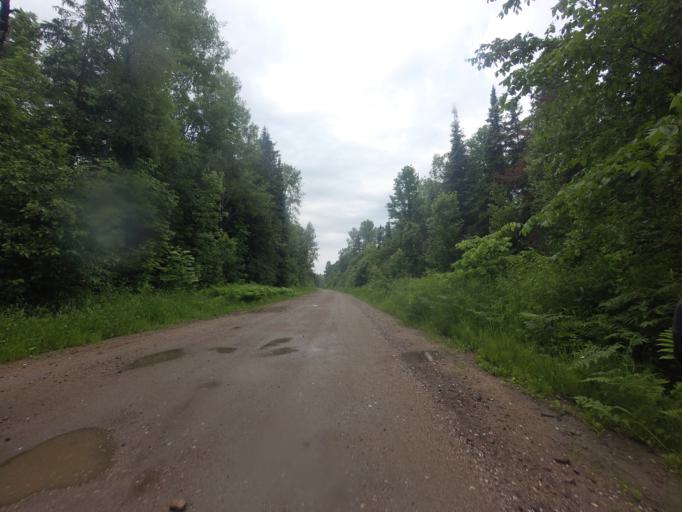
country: CA
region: Quebec
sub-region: Outaouais
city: Maniwaki
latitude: 46.3309
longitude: -76.0047
